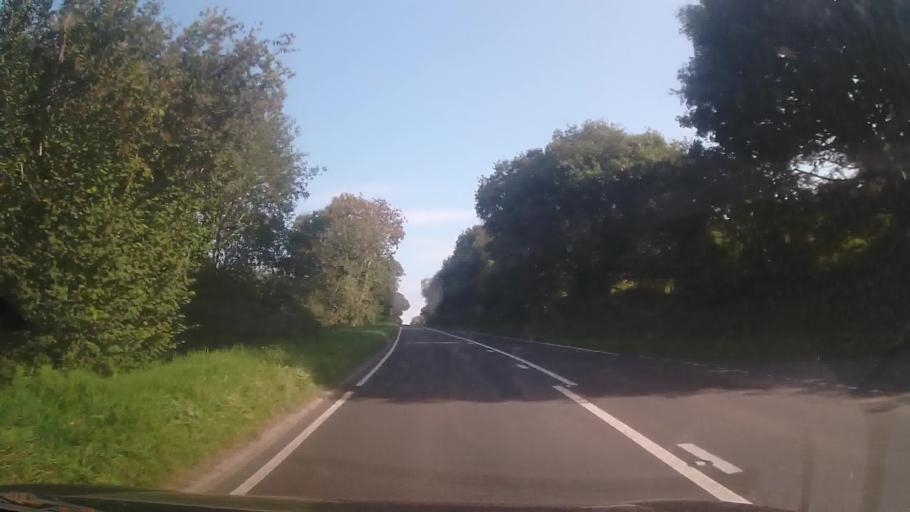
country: GB
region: Wales
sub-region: Pembrokeshire
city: Nevern
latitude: 52.0130
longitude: -4.7562
